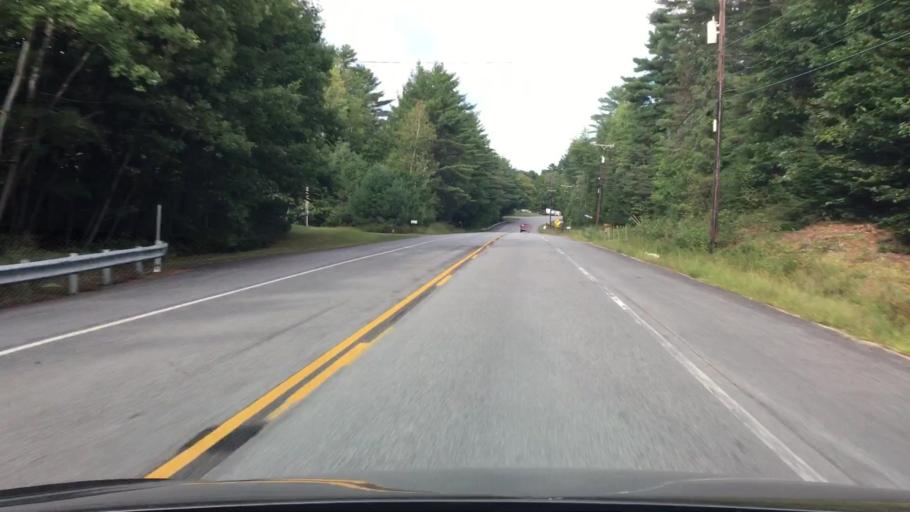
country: US
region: Maine
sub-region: Cumberland County
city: Bridgton
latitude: 44.0686
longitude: -70.7829
